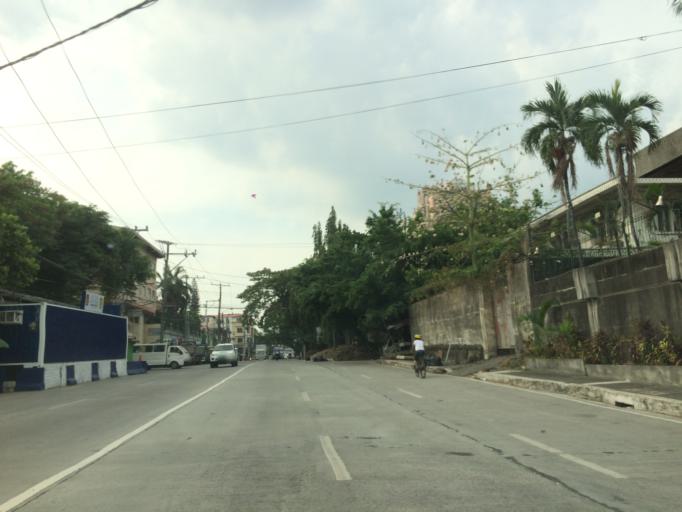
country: PH
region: Calabarzon
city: Del Monte
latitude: 14.6330
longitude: 121.0069
